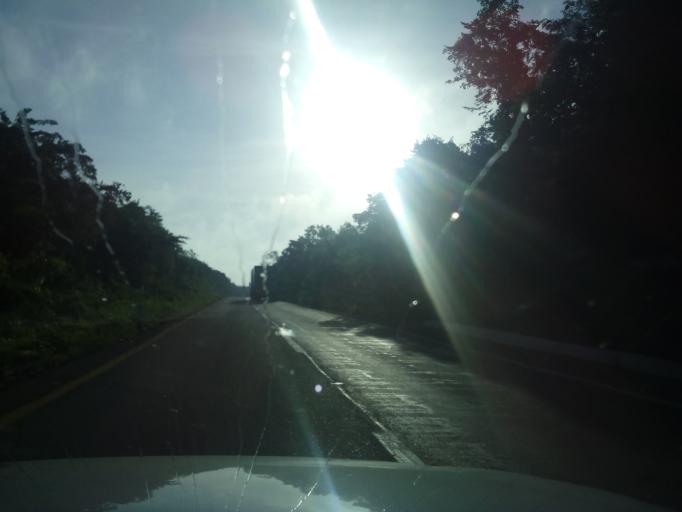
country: MX
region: Yucatan
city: Tunkas
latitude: 20.7657
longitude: -88.8035
